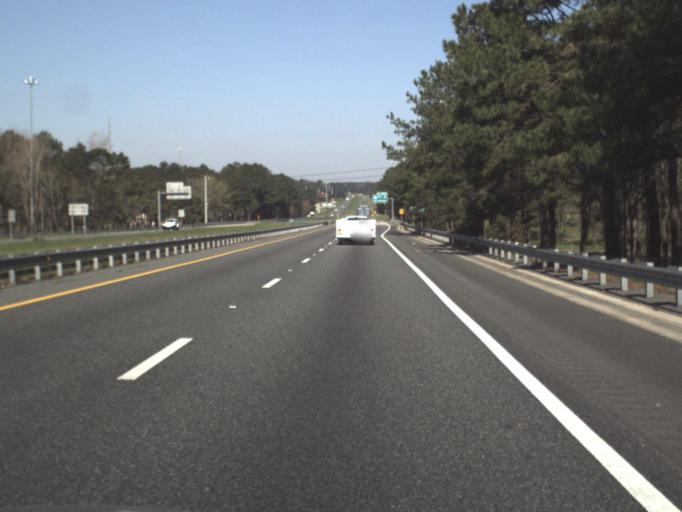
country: US
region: Florida
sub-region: Leon County
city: Tallahassee
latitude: 30.4840
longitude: -84.1562
